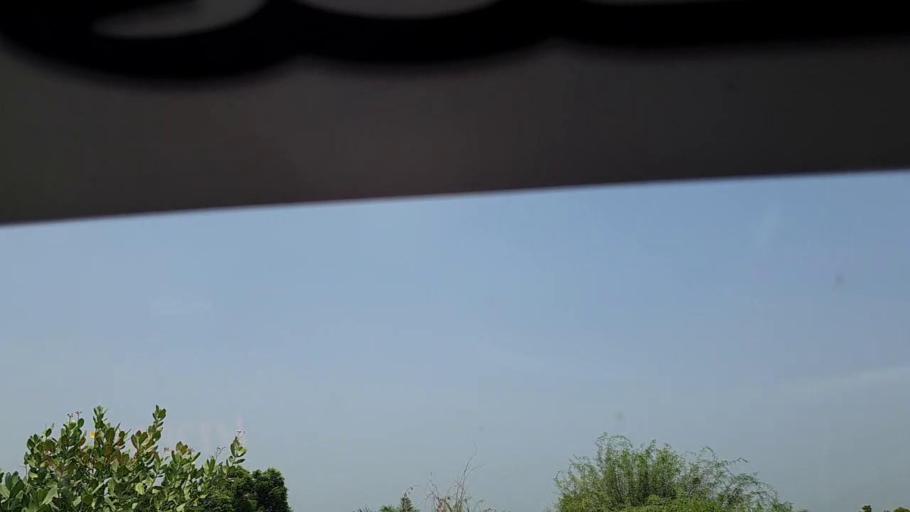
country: PK
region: Sindh
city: Adilpur
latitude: 27.8844
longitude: 69.2585
